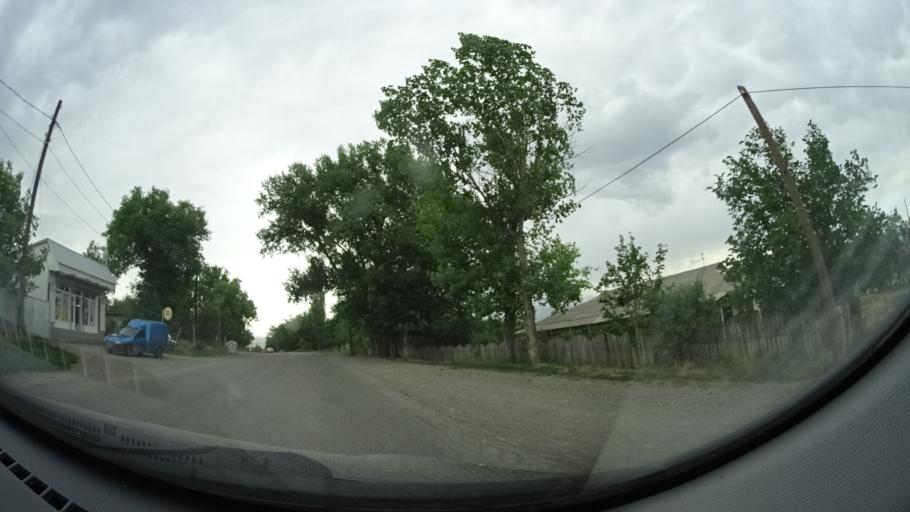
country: GE
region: Samtskhe-Javakheti
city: Akhaltsikhe
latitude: 41.6363
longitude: 43.0396
